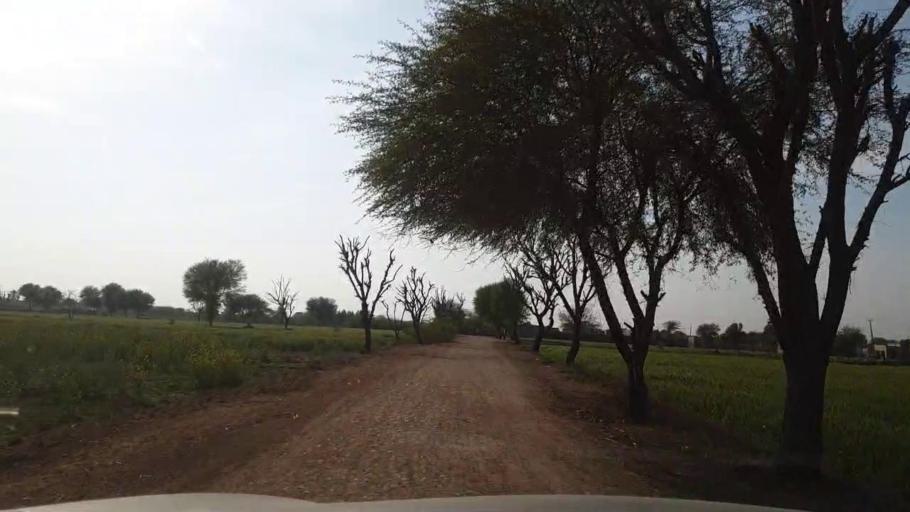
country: PK
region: Sindh
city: Berani
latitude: 25.7154
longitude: 68.8065
